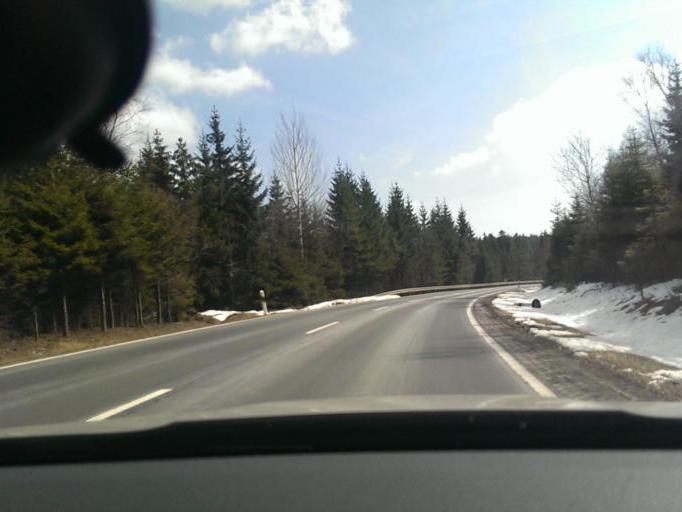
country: DE
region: Thuringia
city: Oberhof
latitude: 50.7150
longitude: 10.7325
